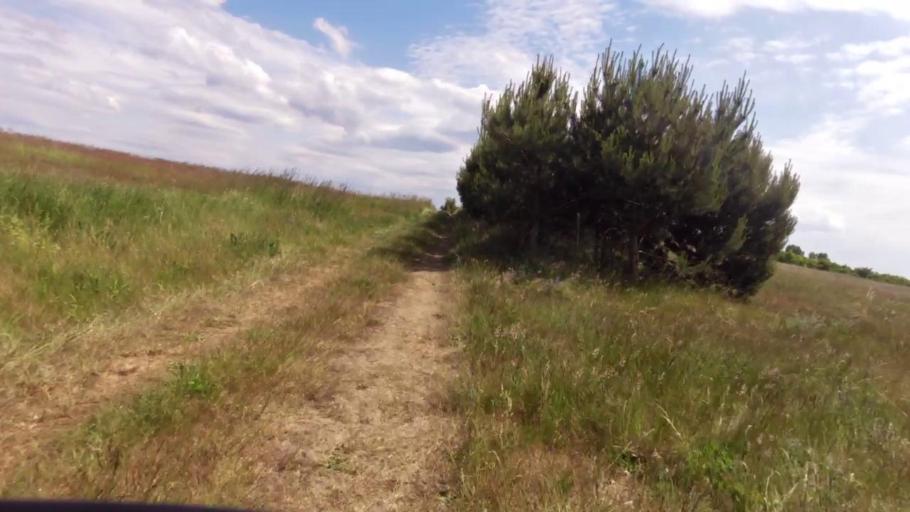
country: PL
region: West Pomeranian Voivodeship
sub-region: Powiat kamienski
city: Wolin
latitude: 53.8525
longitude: 14.5726
